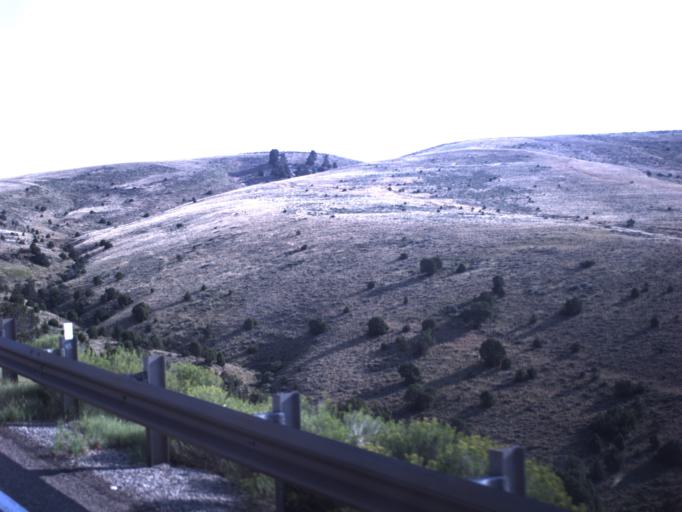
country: US
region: Utah
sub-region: Uintah County
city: Vernal
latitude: 40.6485
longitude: -109.4885
